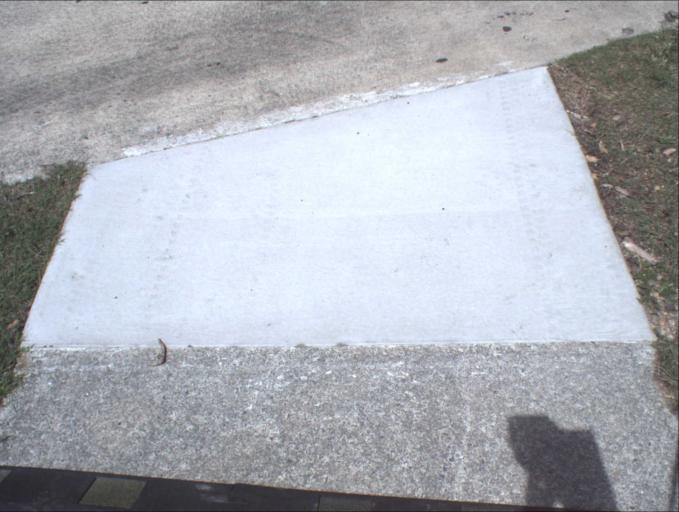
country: AU
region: Queensland
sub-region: Logan
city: Cedar Vale
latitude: -27.8299
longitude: 153.0251
